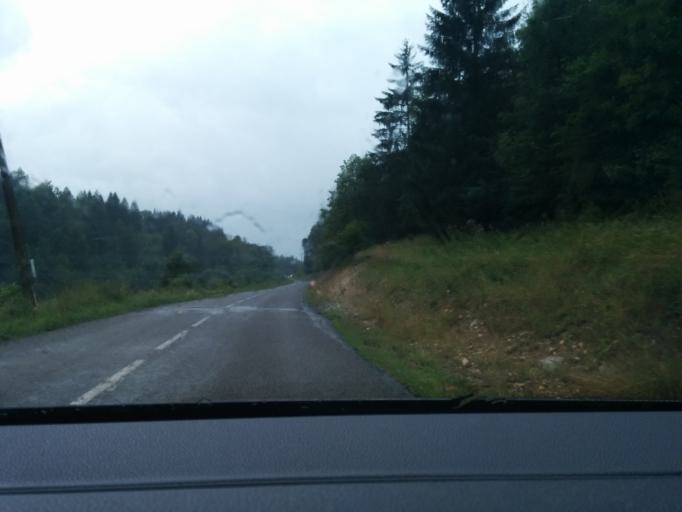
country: FR
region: Franche-Comte
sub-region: Departement du Jura
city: Valfin-les-Saint-Claude
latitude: 46.4467
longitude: 5.8241
